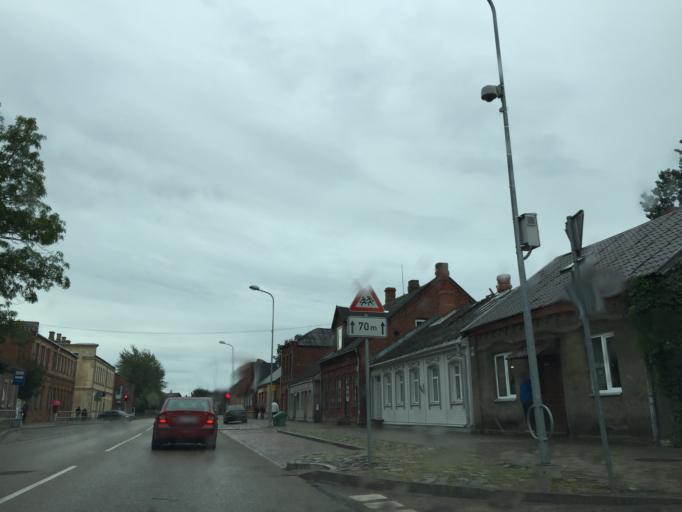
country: LV
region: Jekabpils Rajons
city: Jekabpils
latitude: 56.5047
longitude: 25.8654
